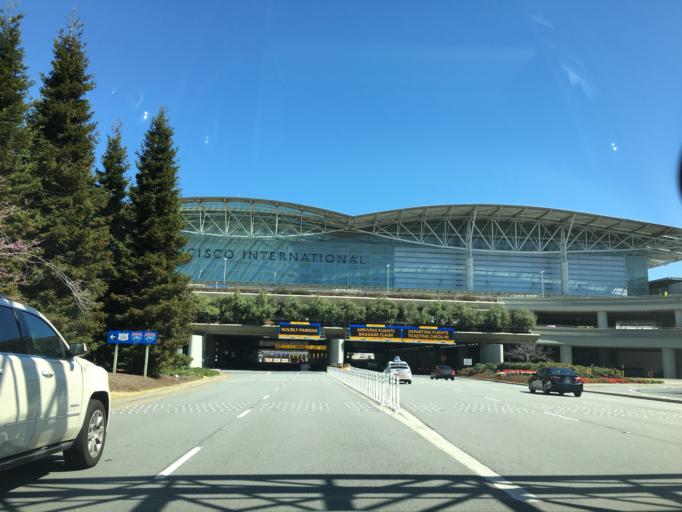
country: US
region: California
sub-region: San Mateo County
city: Millbrae
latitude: 37.6149
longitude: -122.3914
